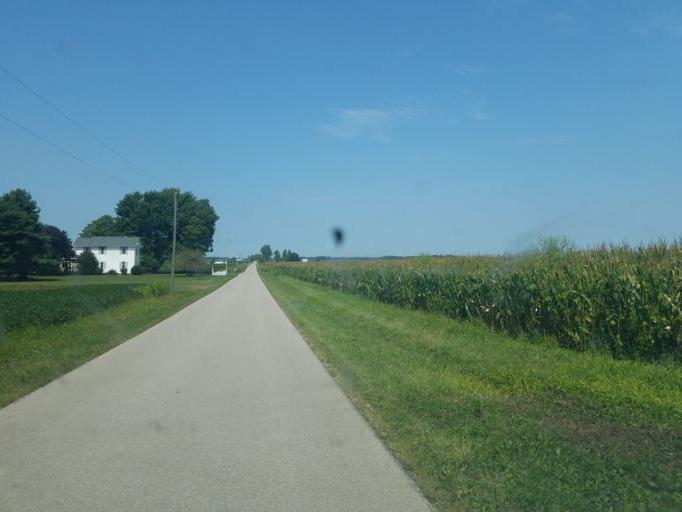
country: US
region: Ohio
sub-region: Crawford County
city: Bucyrus
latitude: 40.7570
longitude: -83.1118
